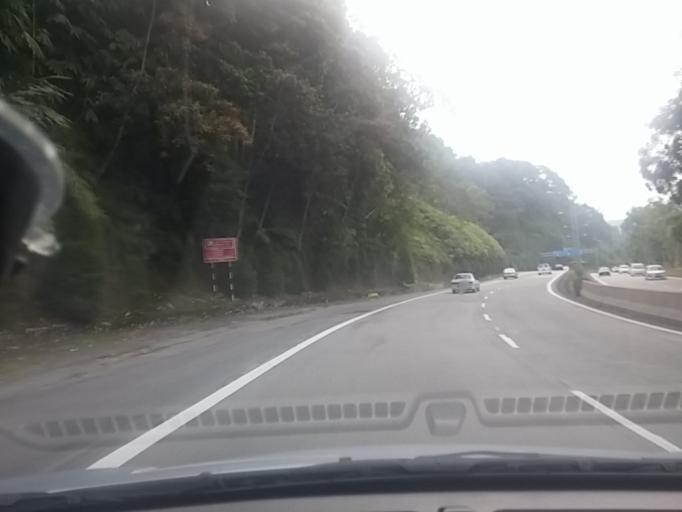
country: MY
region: Pahang
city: Kampung Bukit Tinggi, Bentong
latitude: 3.3773
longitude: 101.7735
